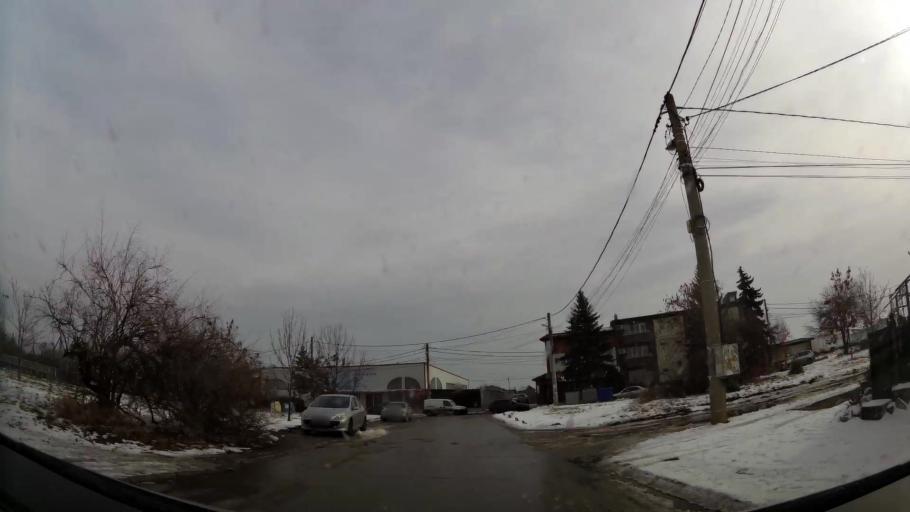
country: BG
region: Sofia-Capital
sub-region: Stolichna Obshtina
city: Sofia
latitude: 42.7110
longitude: 23.4078
